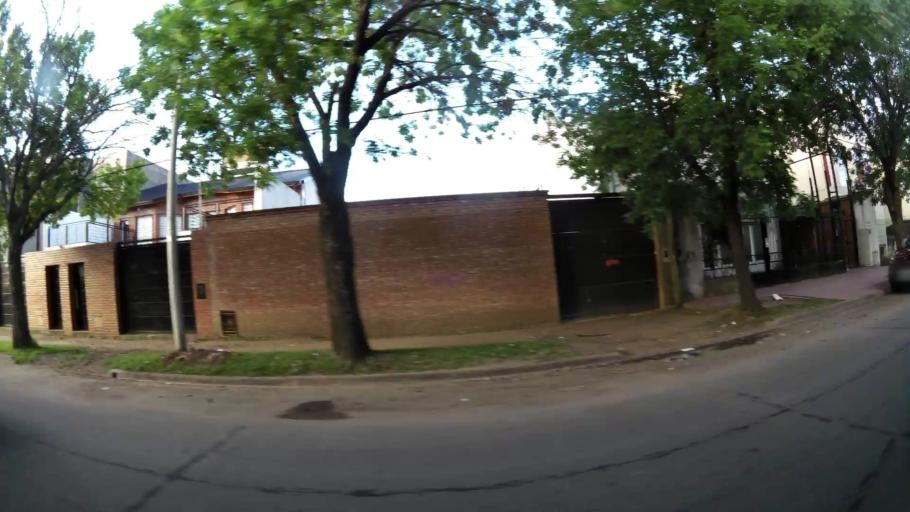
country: AR
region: Santa Fe
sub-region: Departamento de Rosario
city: Rosario
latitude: -32.9755
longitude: -60.6662
